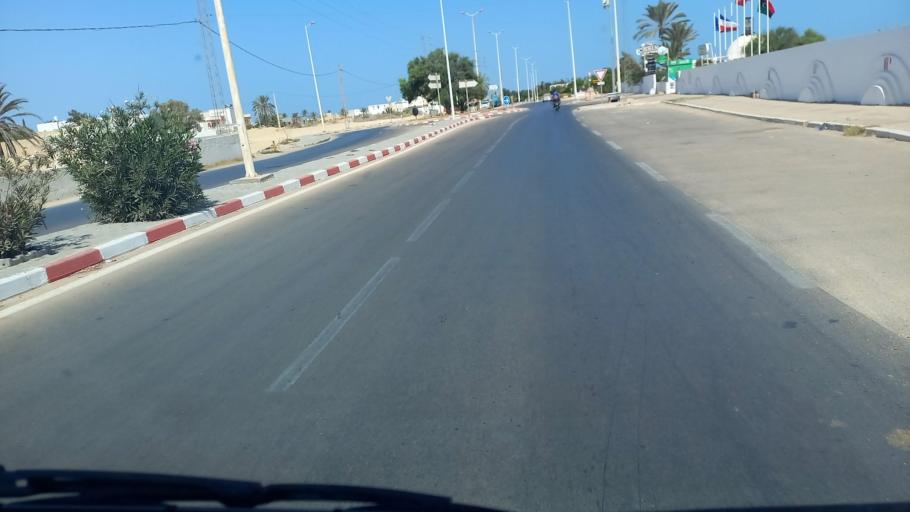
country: TN
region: Madanin
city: Midoun
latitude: 33.8573
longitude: 10.9762
